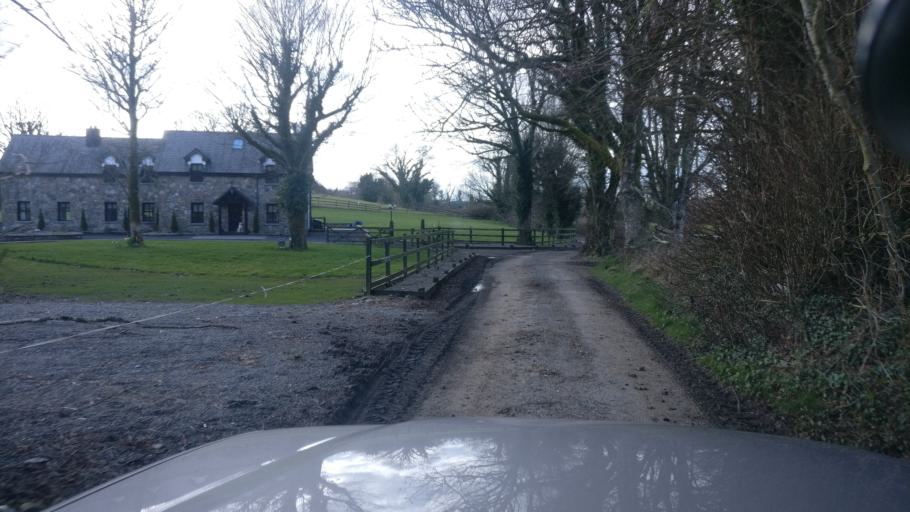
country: IE
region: Connaught
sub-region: County Galway
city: Loughrea
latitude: 53.1829
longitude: -8.4283
